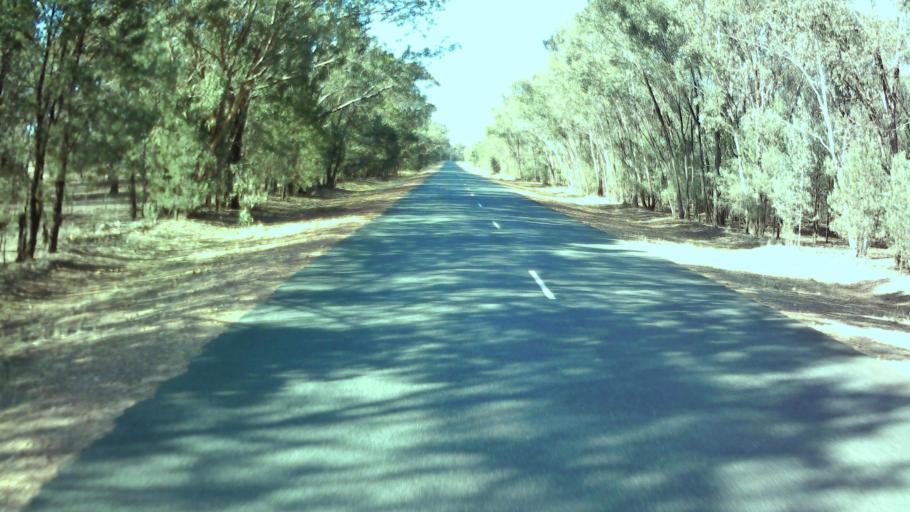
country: AU
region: New South Wales
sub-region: Weddin
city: Grenfell
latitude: -34.0248
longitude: 148.0980
